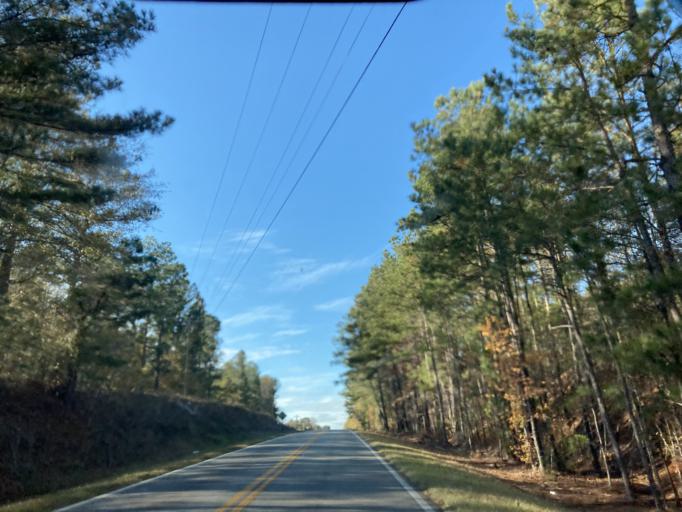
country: US
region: Georgia
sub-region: Jones County
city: Gray
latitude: 32.8901
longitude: -83.5042
